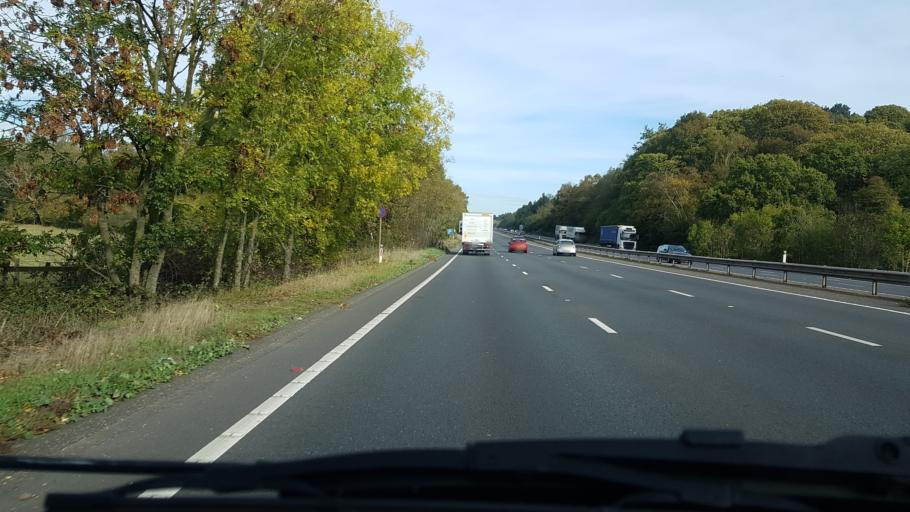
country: GB
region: England
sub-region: Surrey
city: Ripley
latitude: 51.2973
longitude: -0.4855
